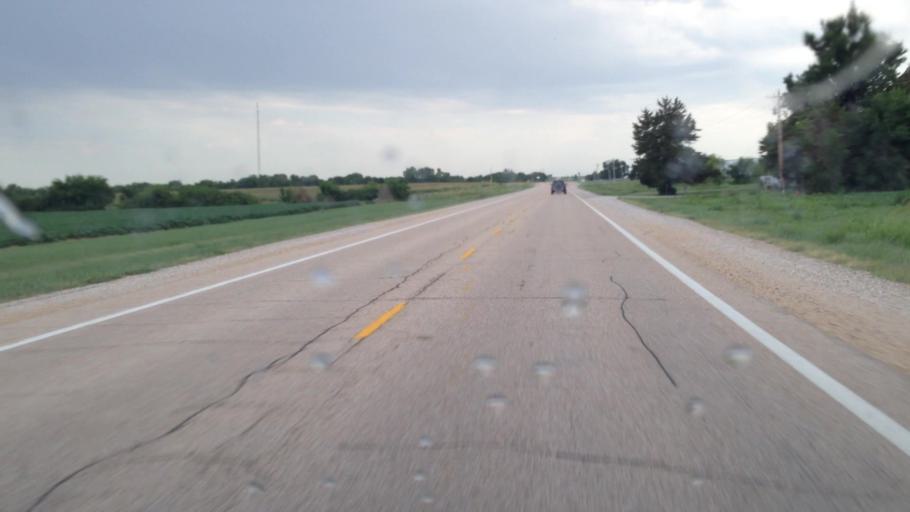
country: US
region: Kansas
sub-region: Coffey County
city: Burlington
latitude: 38.1748
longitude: -95.7389
